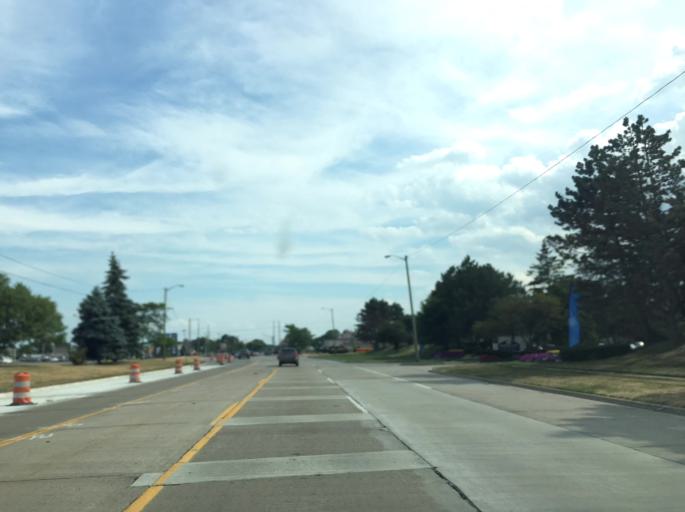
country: US
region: Michigan
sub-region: Macomb County
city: Fraser
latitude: 42.5403
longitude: -82.9893
